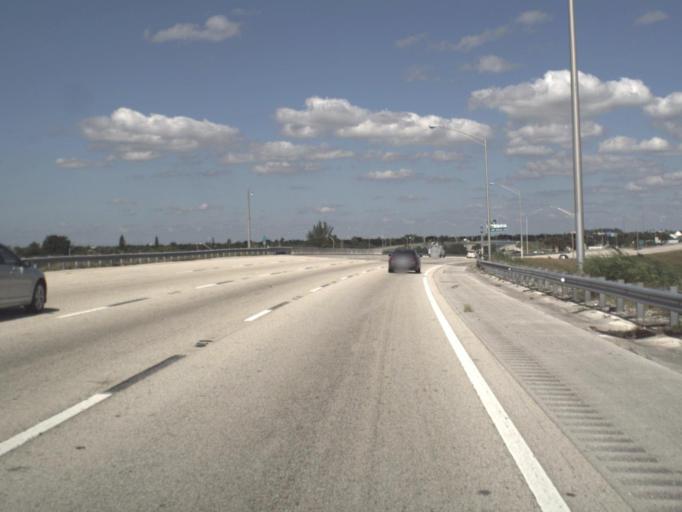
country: US
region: Florida
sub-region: Miami-Dade County
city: Three Lakes
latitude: 25.6514
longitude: -80.3852
